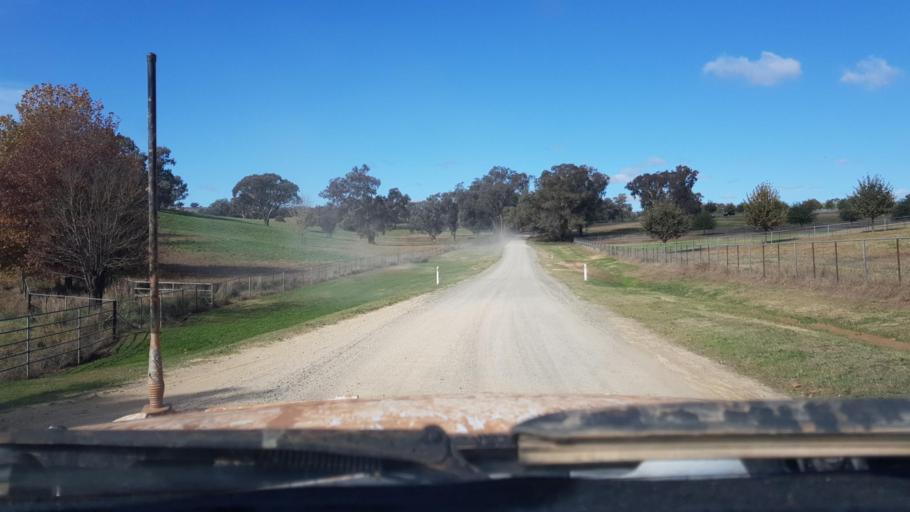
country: AU
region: New South Wales
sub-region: Boorowa
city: Boorowa
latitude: -34.1486
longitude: 148.8130
